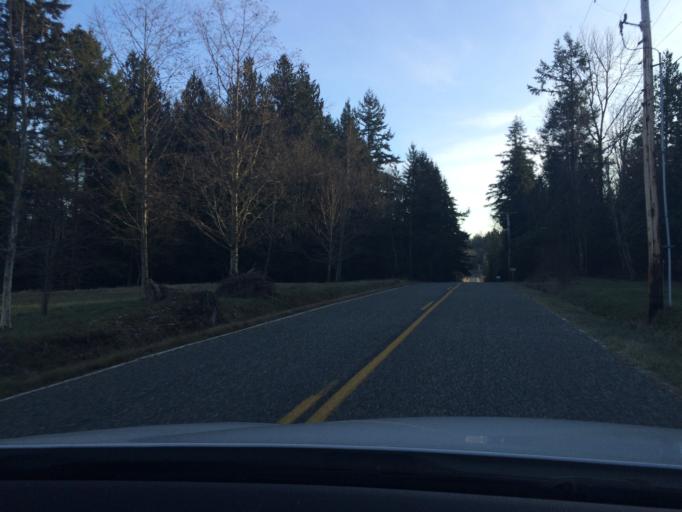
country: US
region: Washington
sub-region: Whatcom County
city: Everson
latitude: 48.8583
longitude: -122.3982
